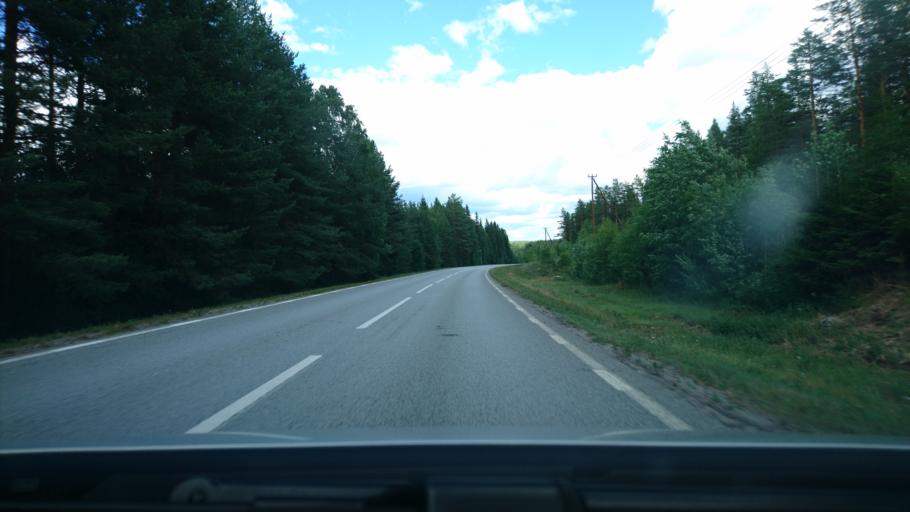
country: SE
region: Vaesternorrland
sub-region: Solleftea Kommun
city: As
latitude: 63.7021
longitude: 16.9153
